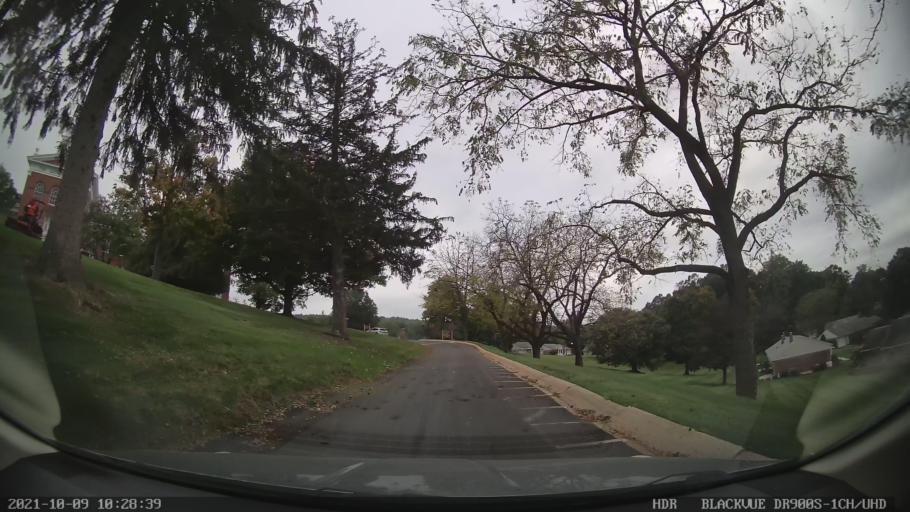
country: US
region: Pennsylvania
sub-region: Berks County
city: Topton
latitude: 40.4965
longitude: -75.6991
